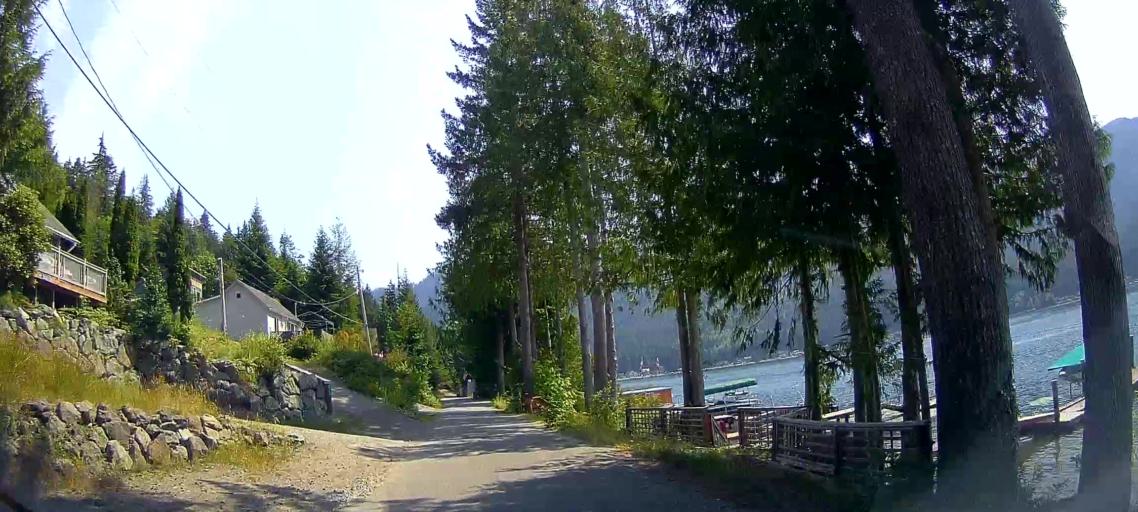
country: US
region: Washington
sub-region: Snohomish County
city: Arlington Heights
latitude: 48.3262
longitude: -122.0078
